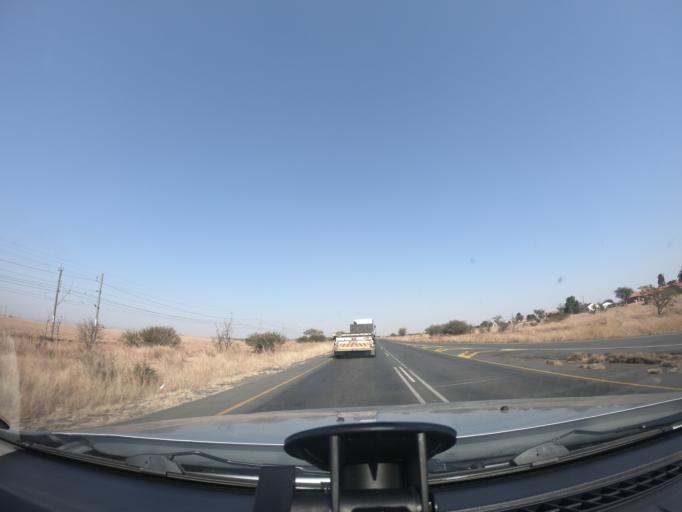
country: ZA
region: KwaZulu-Natal
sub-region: uThukela District Municipality
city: Ladysmith
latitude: -28.7551
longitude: 29.8224
